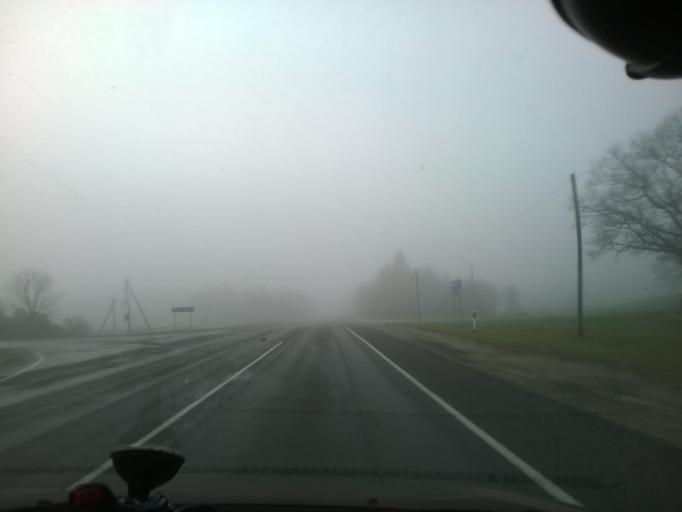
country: EE
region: Tartu
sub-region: Elva linn
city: Elva
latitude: 58.1249
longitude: 26.5202
